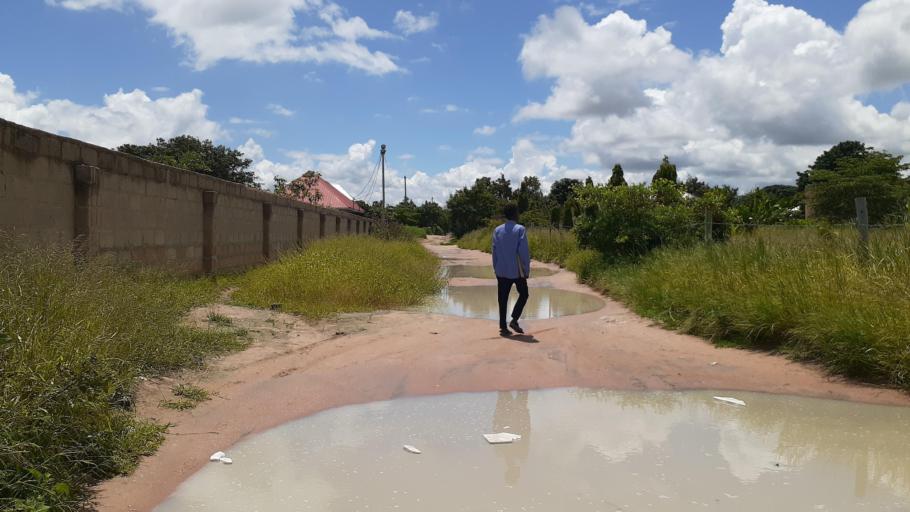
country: TZ
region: Dodoma
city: Dodoma
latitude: -6.1191
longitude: 35.7426
